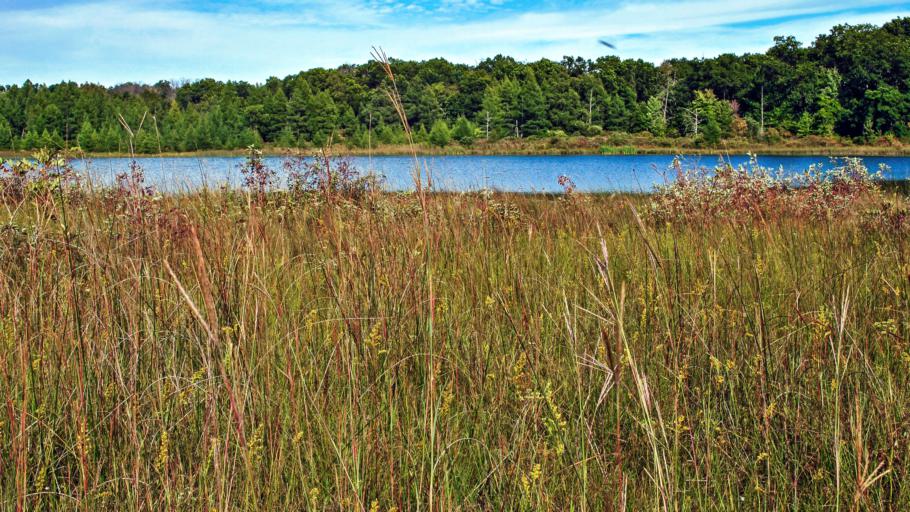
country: US
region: Wisconsin
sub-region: Marquette County
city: Montello
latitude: 43.6862
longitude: -89.3915
